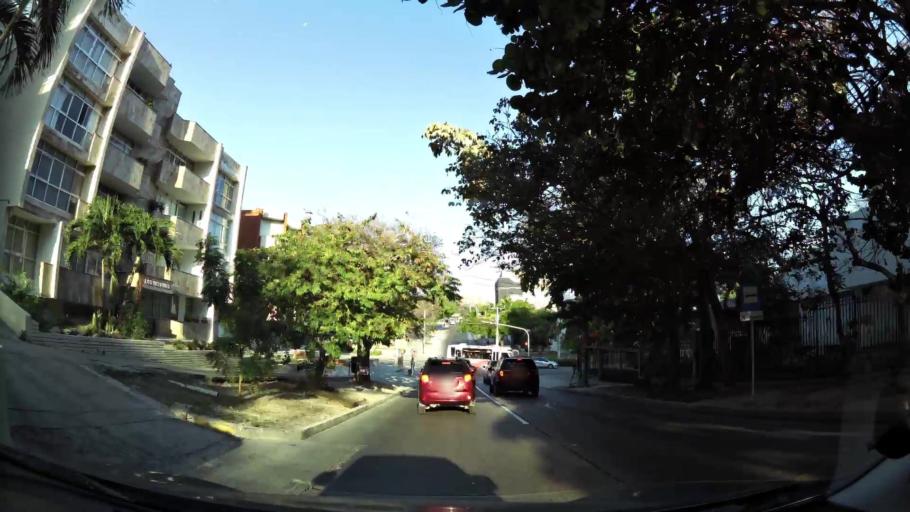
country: CO
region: Atlantico
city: Barranquilla
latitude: 11.0071
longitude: -74.8156
